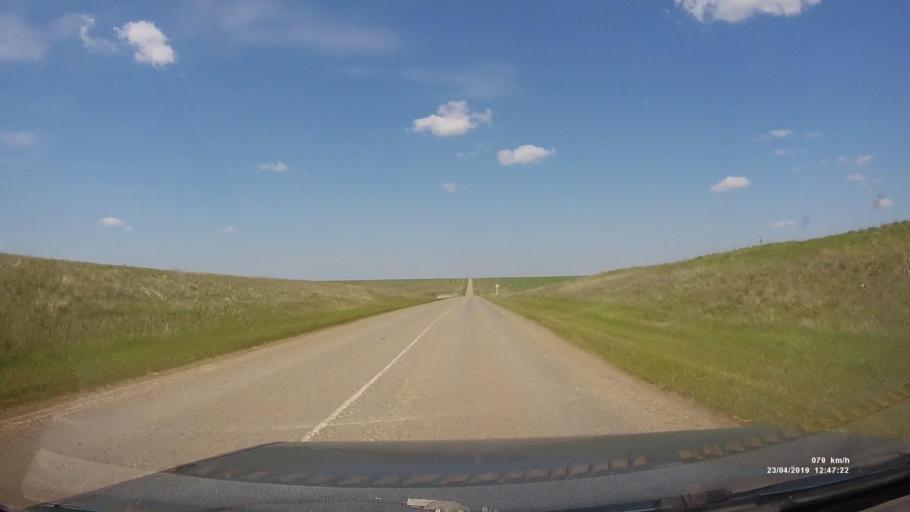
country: RU
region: Kalmykiya
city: Yashalta
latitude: 46.5114
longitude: 42.6386
